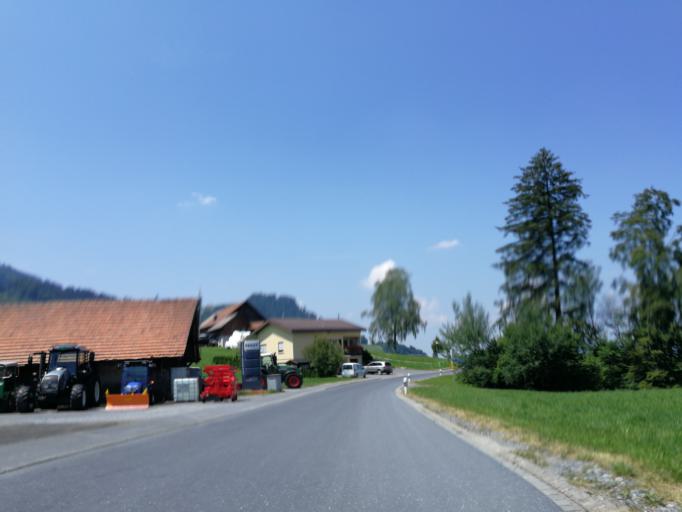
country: CH
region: Schwyz
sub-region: Bezirk Hoefe
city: Schindellegi
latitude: 47.1753
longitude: 8.7264
